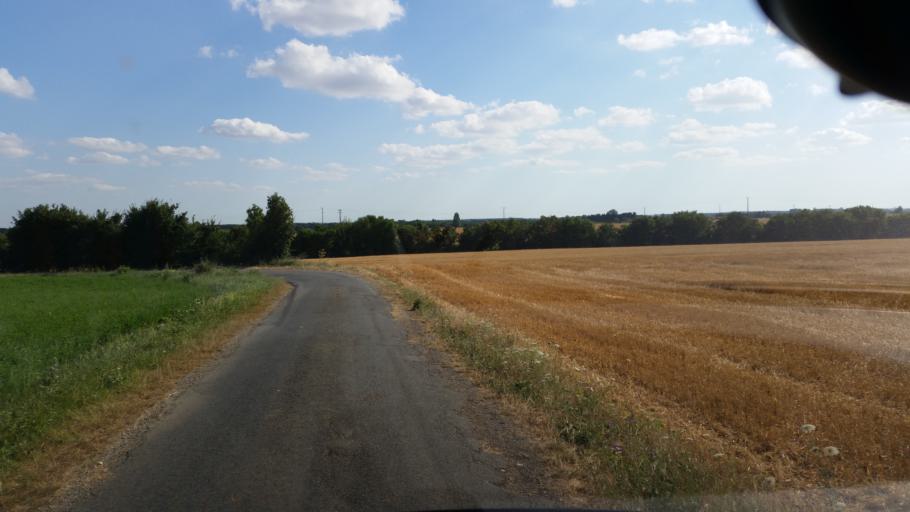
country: FR
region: Poitou-Charentes
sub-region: Departement de la Charente-Maritime
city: Saint-Jean-de-Liversay
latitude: 46.2325
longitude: -0.8900
